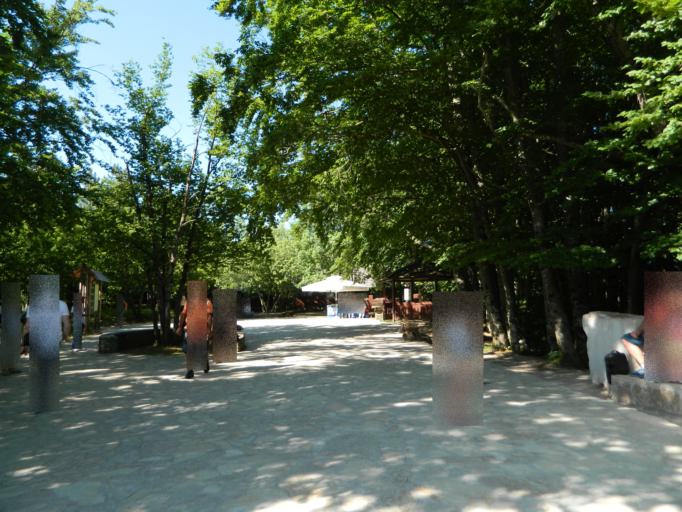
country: HR
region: Licko-Senjska
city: Jezerce
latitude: 44.9043
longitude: 15.6110
